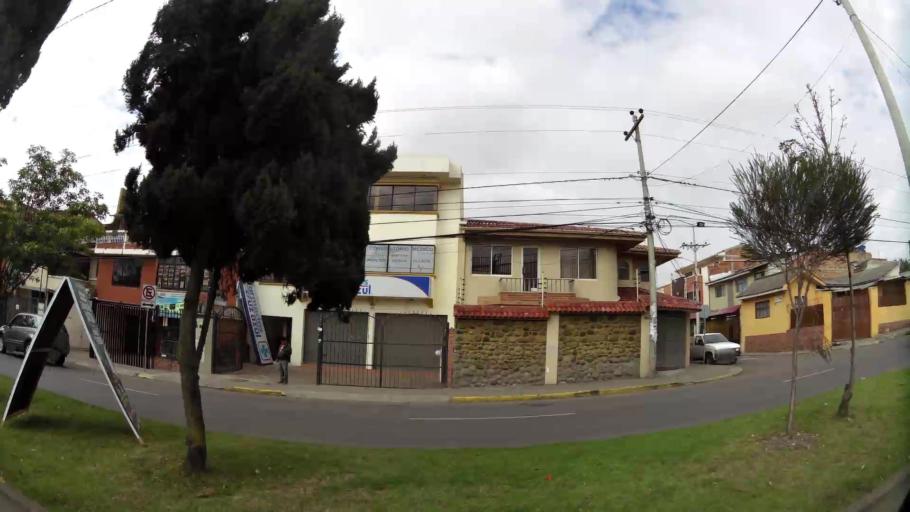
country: EC
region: Azuay
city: Cuenca
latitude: -2.8900
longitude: -78.9771
